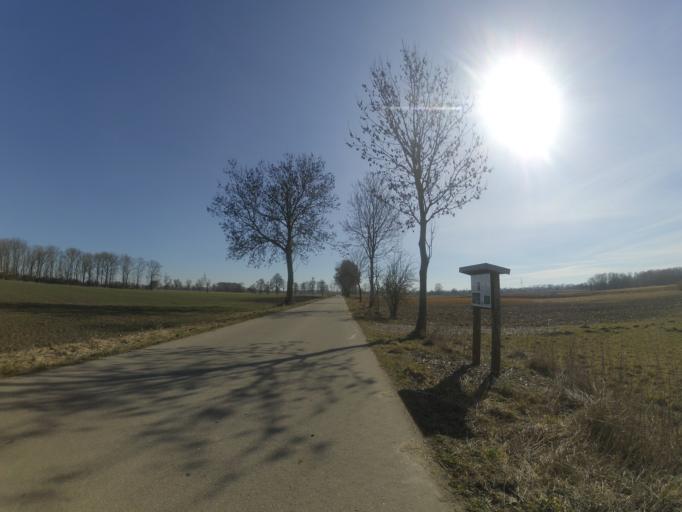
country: DE
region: Baden-Wuerttemberg
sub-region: Tuebingen Region
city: Rammingen
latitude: 48.4992
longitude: 10.1536
